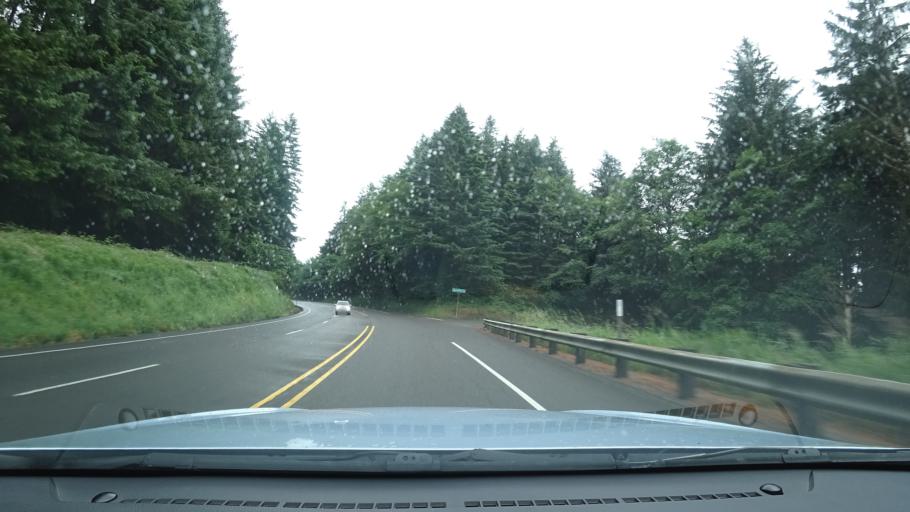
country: US
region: Oregon
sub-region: Douglas County
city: Reedsport
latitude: 43.7534
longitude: -124.1265
